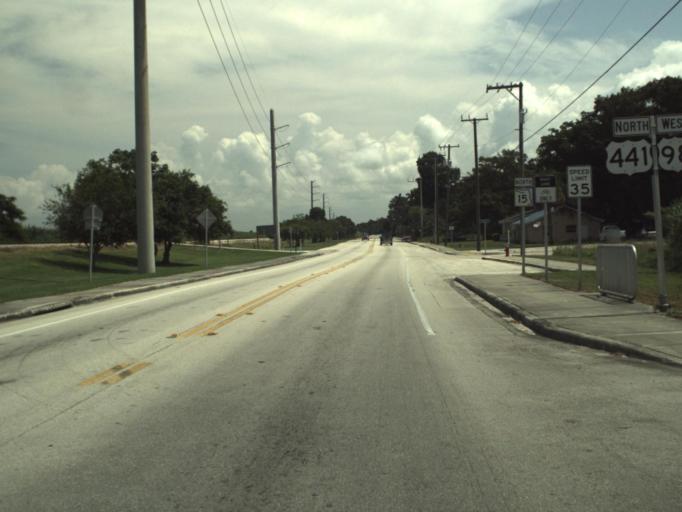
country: US
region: Florida
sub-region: Palm Beach County
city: Pahokee
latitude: 26.8638
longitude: -80.6314
